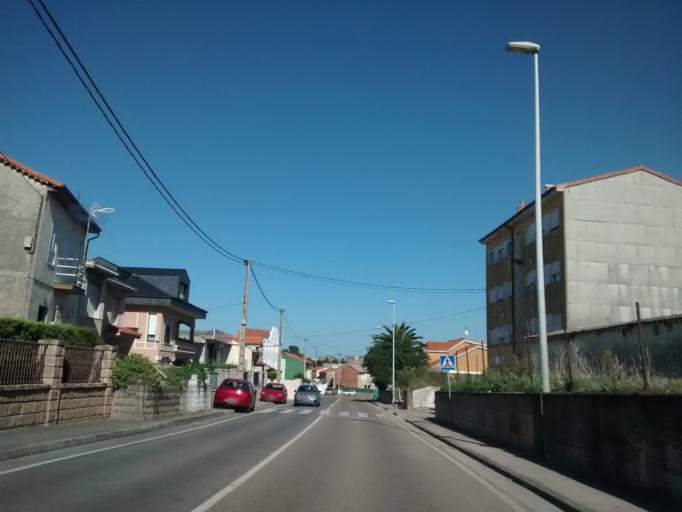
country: ES
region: Cantabria
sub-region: Provincia de Cantabria
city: Santander
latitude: 43.4654
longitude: -3.8454
